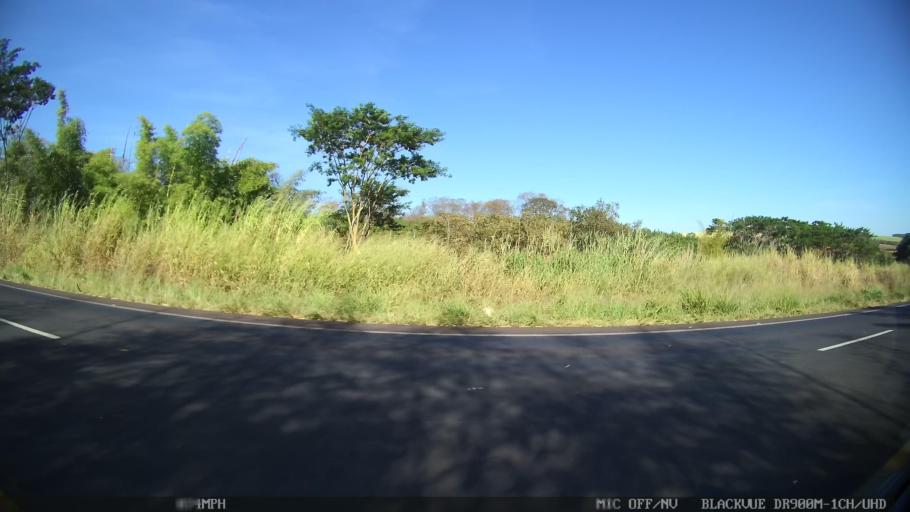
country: BR
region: Sao Paulo
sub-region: Barretos
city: Barretos
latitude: -20.6138
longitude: -48.7568
